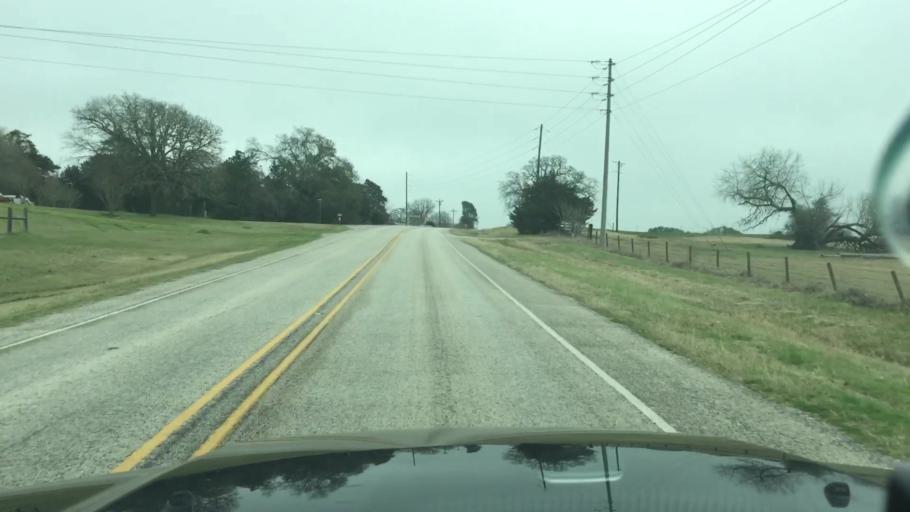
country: US
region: Texas
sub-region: Fayette County
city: La Grange
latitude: 30.0064
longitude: -96.9060
